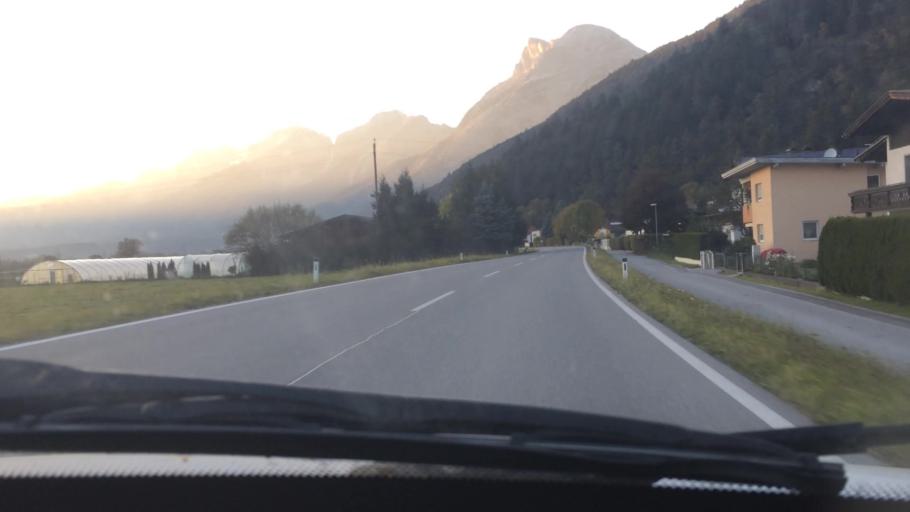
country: AT
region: Tyrol
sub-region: Politischer Bezirk Innsbruck Land
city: Polling in Tirol
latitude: 47.2945
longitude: 11.1523
